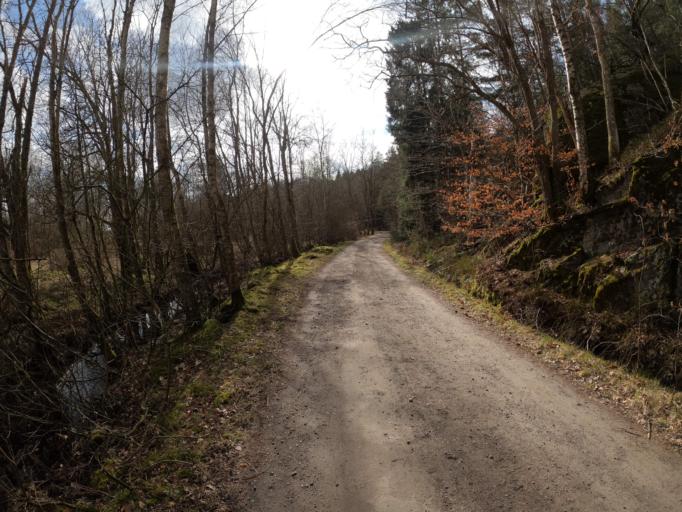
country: SE
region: Vaestra Goetaland
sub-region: Harryda Kommun
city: Molnlycke
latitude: 57.6351
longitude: 12.0997
